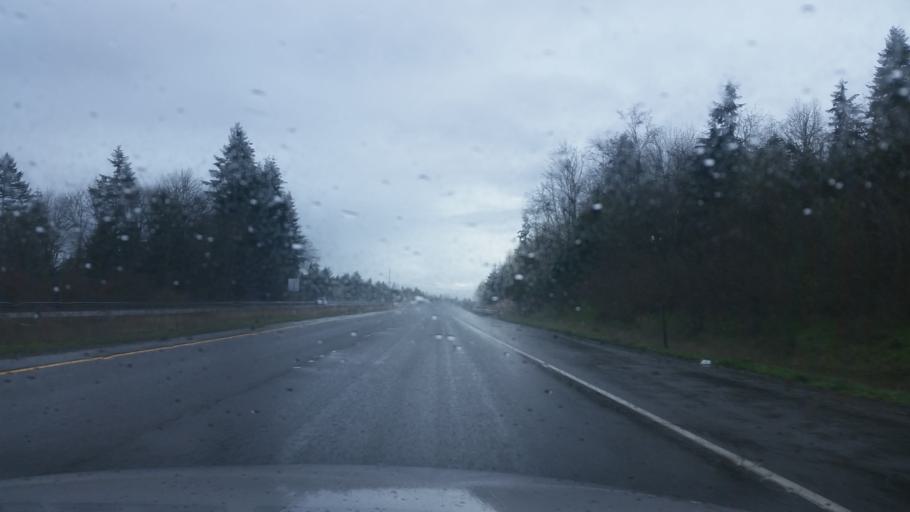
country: US
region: Washington
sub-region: King County
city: Maple Valley
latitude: 47.3897
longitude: -122.0552
